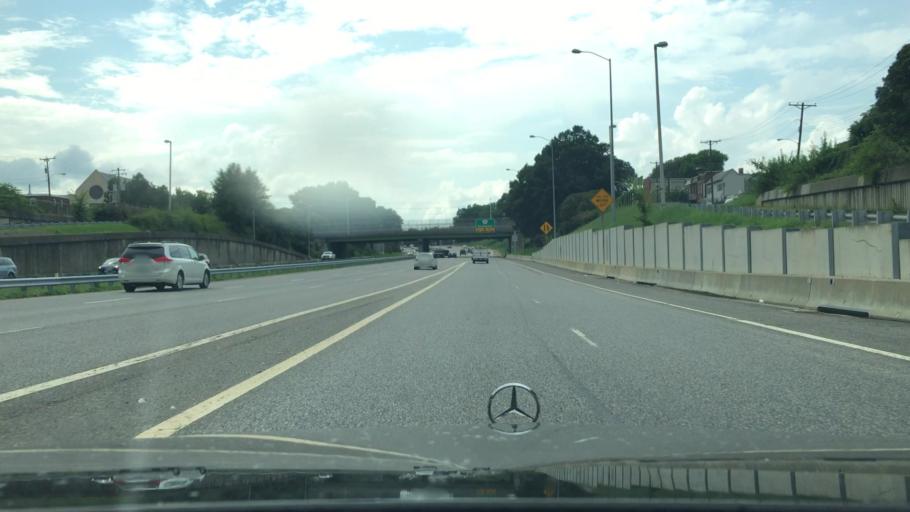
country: US
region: Virginia
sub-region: City of Richmond
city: Richmond
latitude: 37.5463
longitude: -77.4647
